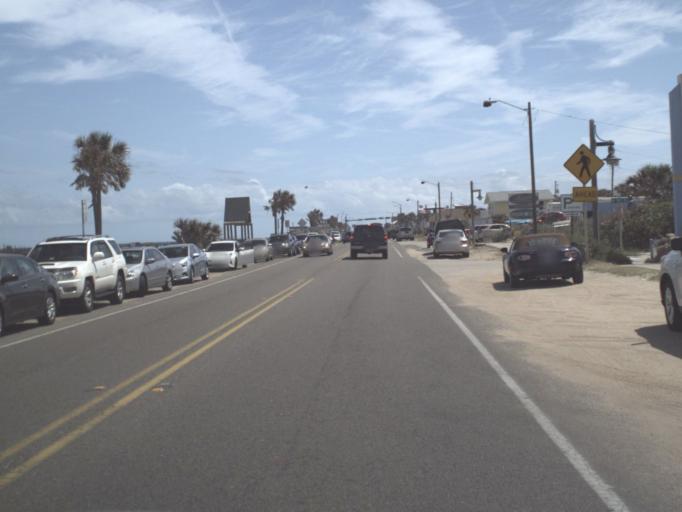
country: US
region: Florida
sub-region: Flagler County
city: Flagler Beach
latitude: 29.4839
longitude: -81.1288
